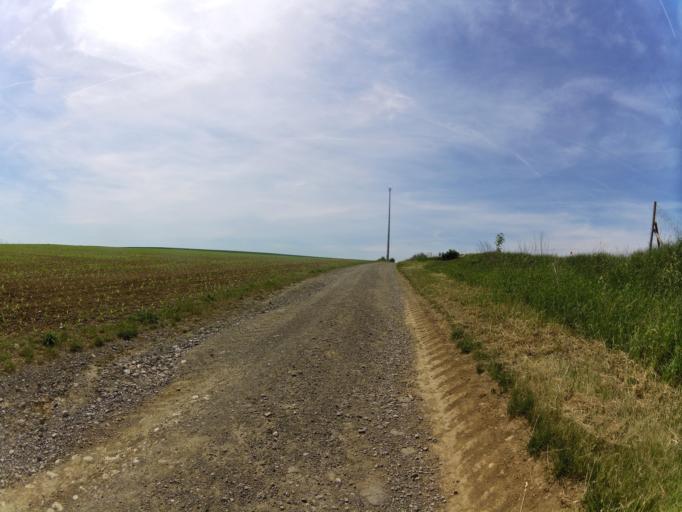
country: DE
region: Bavaria
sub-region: Regierungsbezirk Unterfranken
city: Sommerhausen
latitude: 49.6714
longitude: 10.0304
